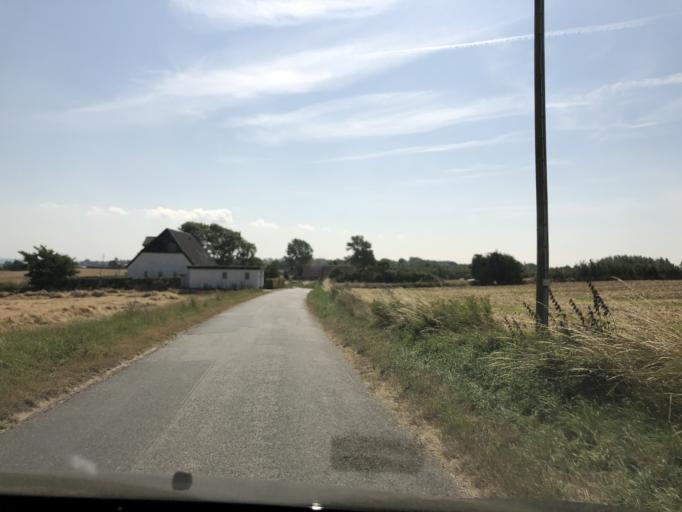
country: DK
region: South Denmark
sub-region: Faaborg-Midtfyn Kommune
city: Faaborg
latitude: 54.9447
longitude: 10.2434
